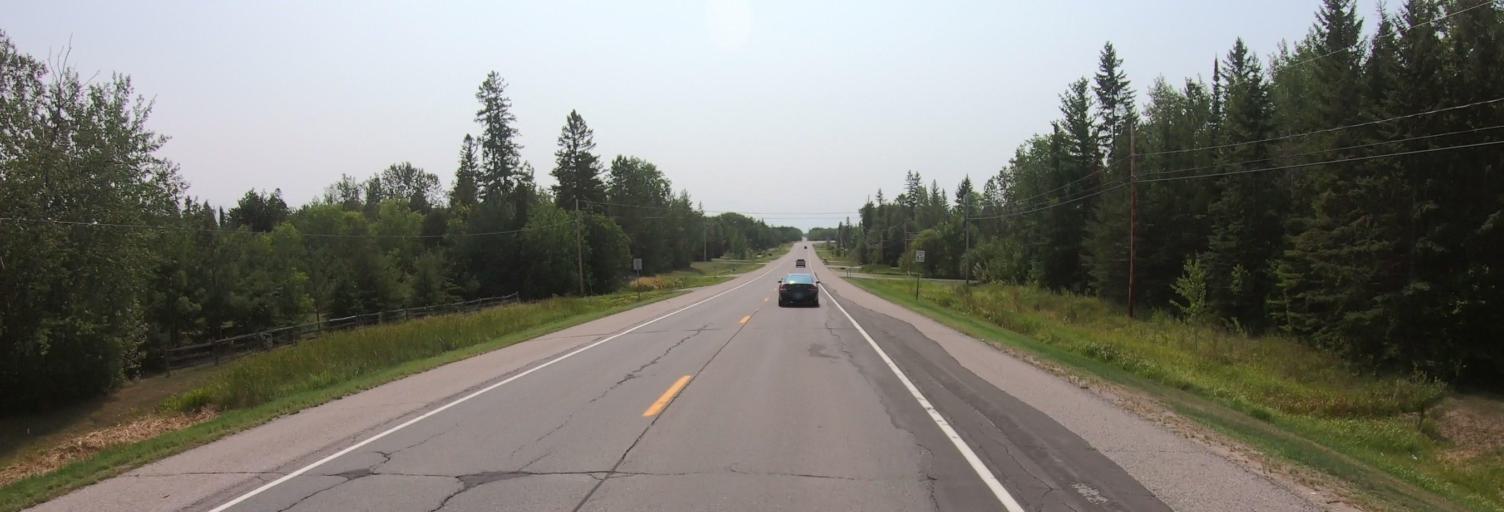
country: US
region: Minnesota
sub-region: Koochiching County
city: International Falls
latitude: 48.5632
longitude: -93.4401
